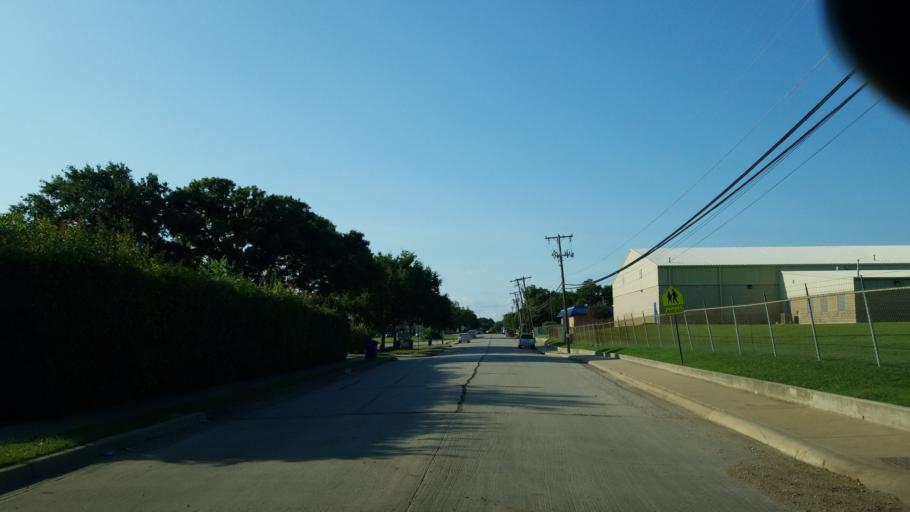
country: US
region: Texas
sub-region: Dallas County
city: Carrollton
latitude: 32.9446
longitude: -96.8976
